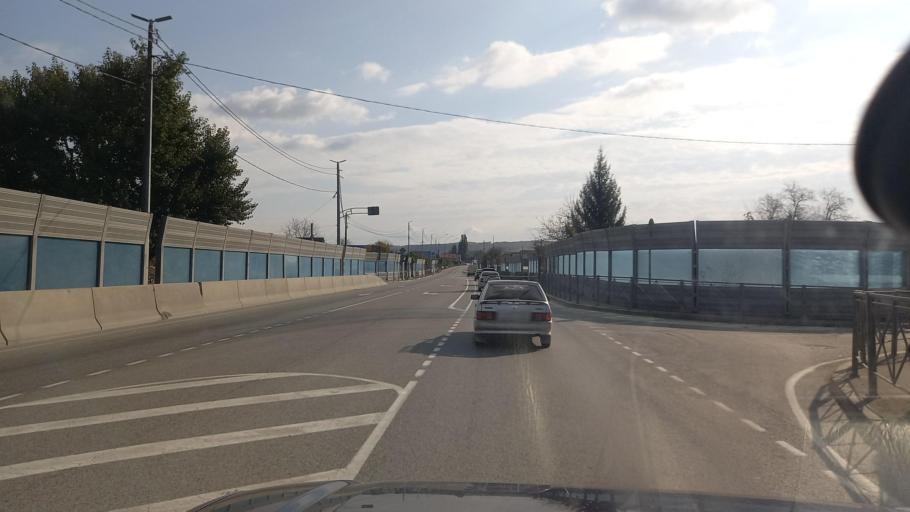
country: RU
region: Krasnodarskiy
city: Krymsk
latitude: 44.8689
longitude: 37.8476
